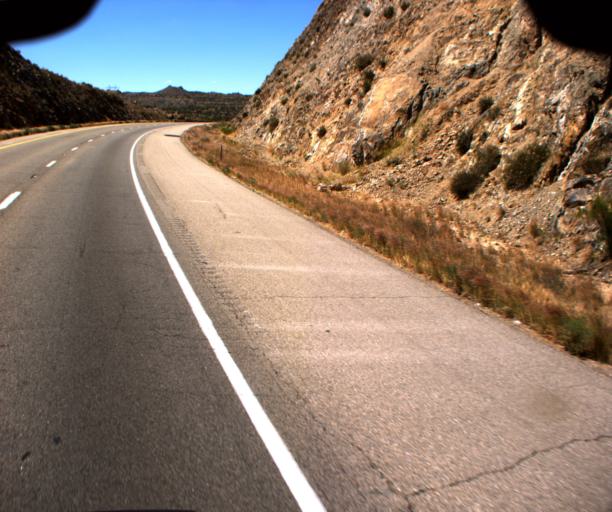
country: US
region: Arizona
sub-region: Yavapai County
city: Bagdad
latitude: 34.4588
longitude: -113.2933
